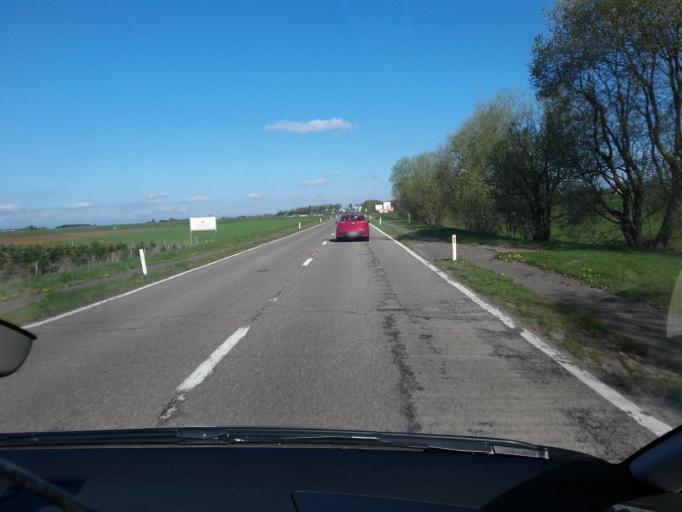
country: BE
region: Wallonia
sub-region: Province du Luxembourg
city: Neufchateau
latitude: 49.8991
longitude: 5.3793
